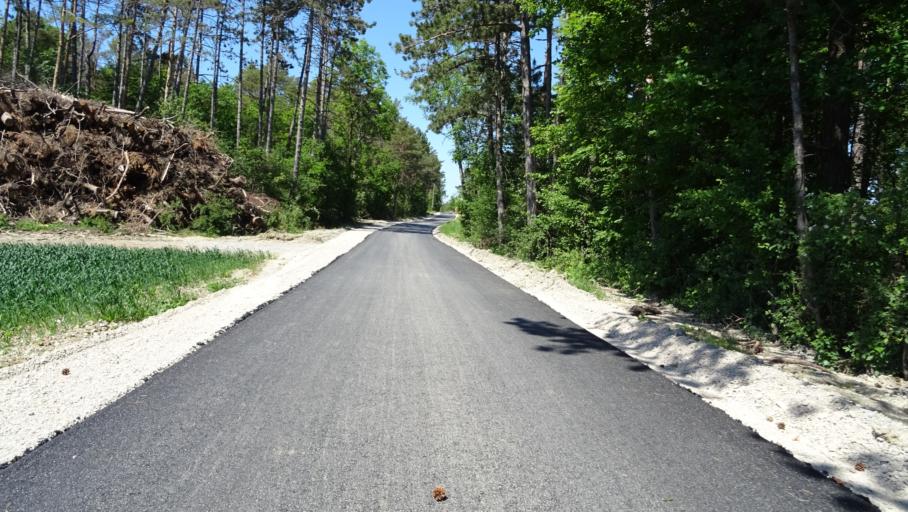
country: DE
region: Baden-Wuerttemberg
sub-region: Karlsruhe Region
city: Buchen
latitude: 49.4856
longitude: 9.3288
